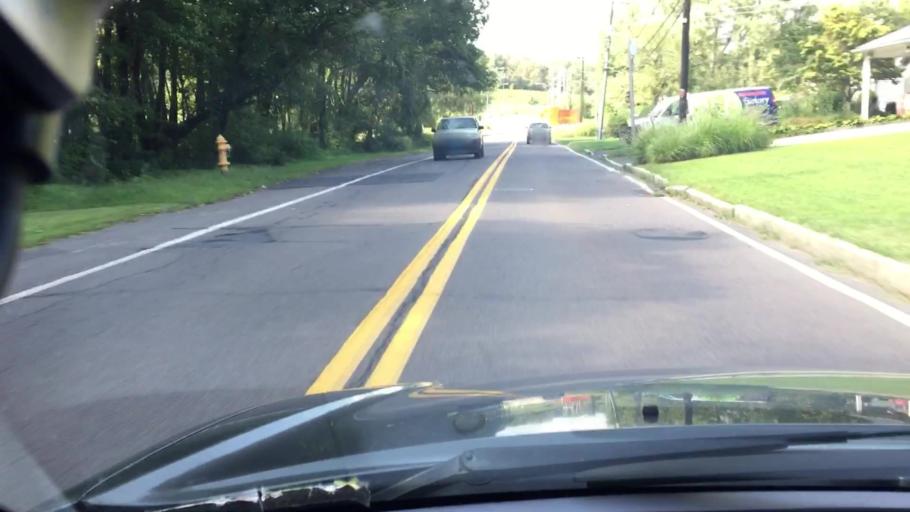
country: US
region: Pennsylvania
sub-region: Luzerne County
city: Nanticoke
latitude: 41.1885
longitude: -75.9879
